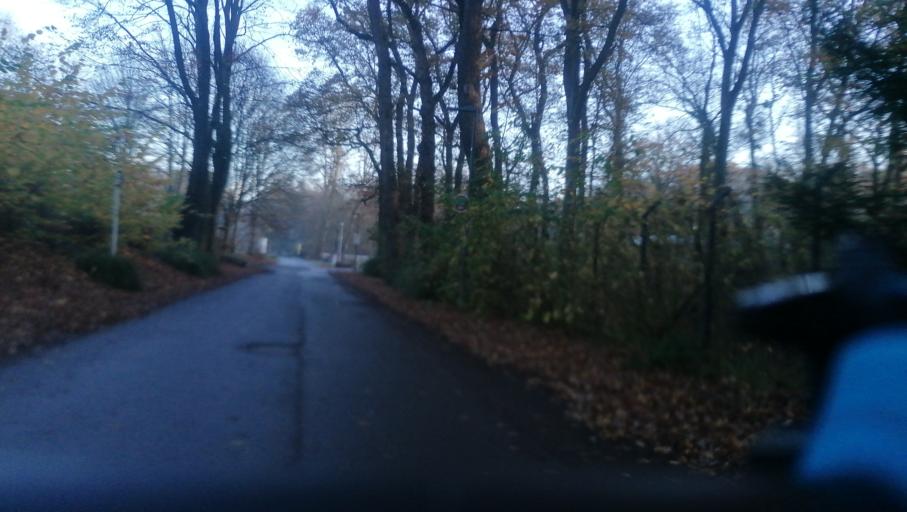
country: DE
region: North Rhine-Westphalia
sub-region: Regierungsbezirk Arnsberg
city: Dortmund
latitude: 51.4736
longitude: 7.4666
